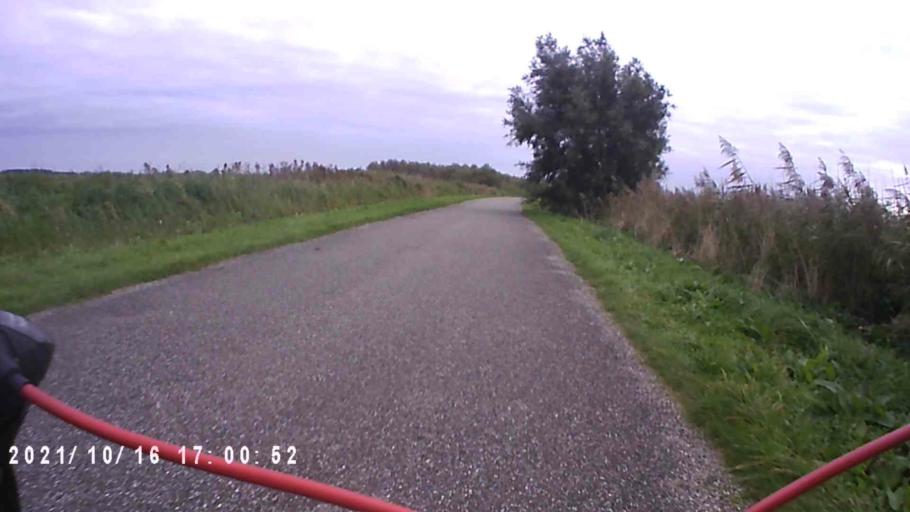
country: NL
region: Friesland
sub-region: Gemeente Dongeradeel
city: Anjum
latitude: 53.3519
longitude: 6.1527
